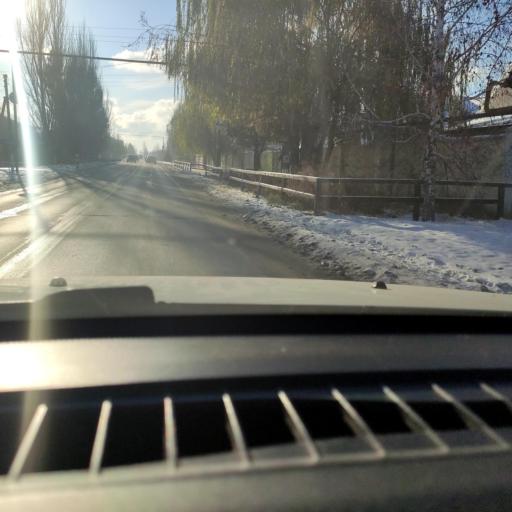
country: RU
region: Samara
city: Podstepki
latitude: 53.5220
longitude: 49.1542
